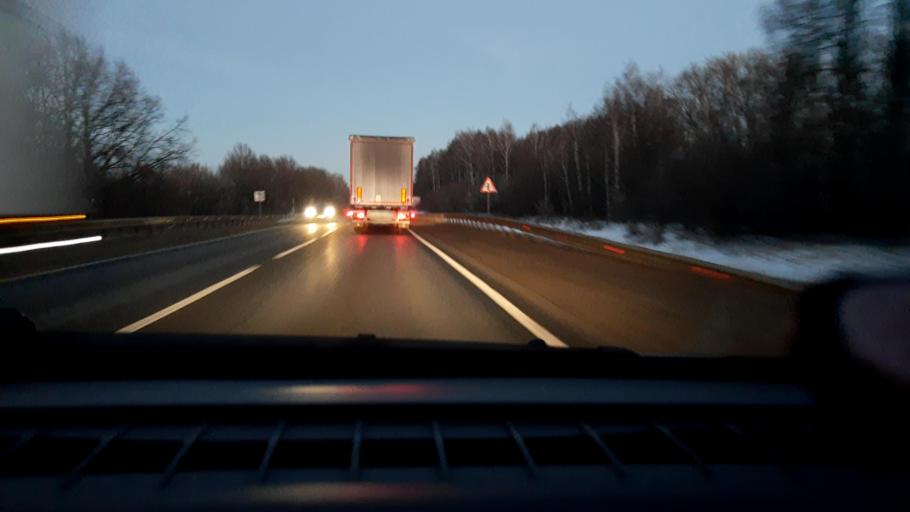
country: RU
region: Nizjnij Novgorod
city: Lyskovo
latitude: 56.0087
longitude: 44.9444
